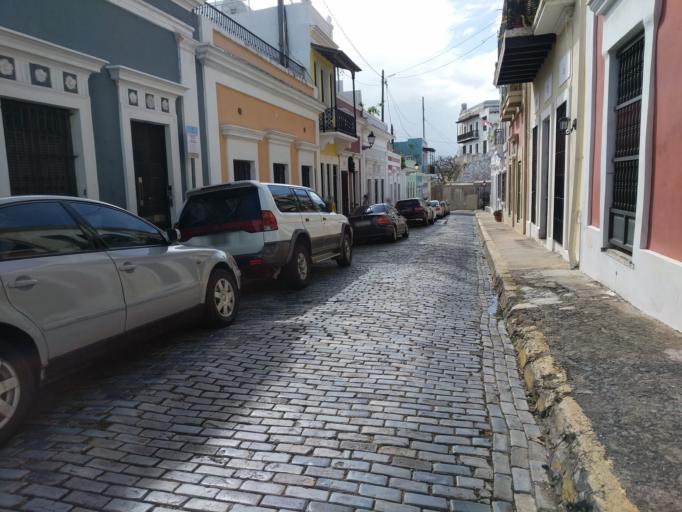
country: PR
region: San Juan
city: San Juan
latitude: 18.4663
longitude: -66.1191
